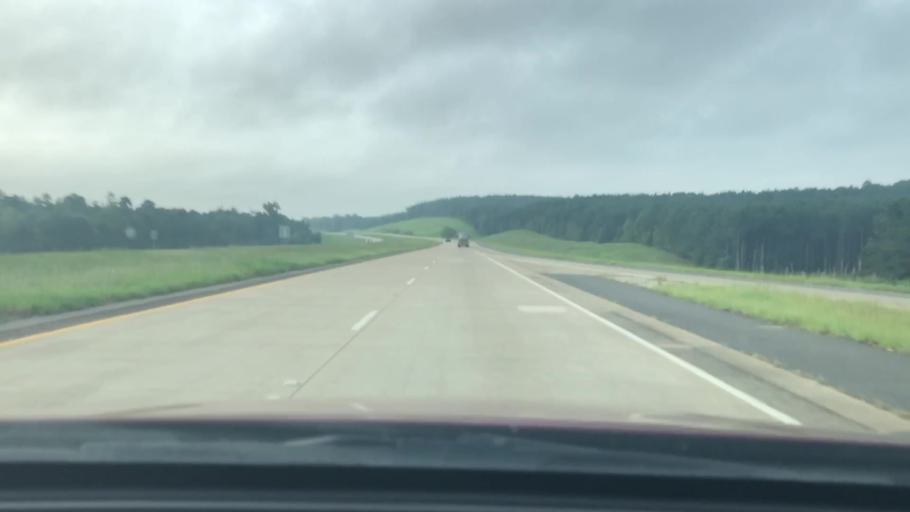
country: US
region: Louisiana
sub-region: Caddo Parish
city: Vivian
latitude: 32.9397
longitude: -93.8976
